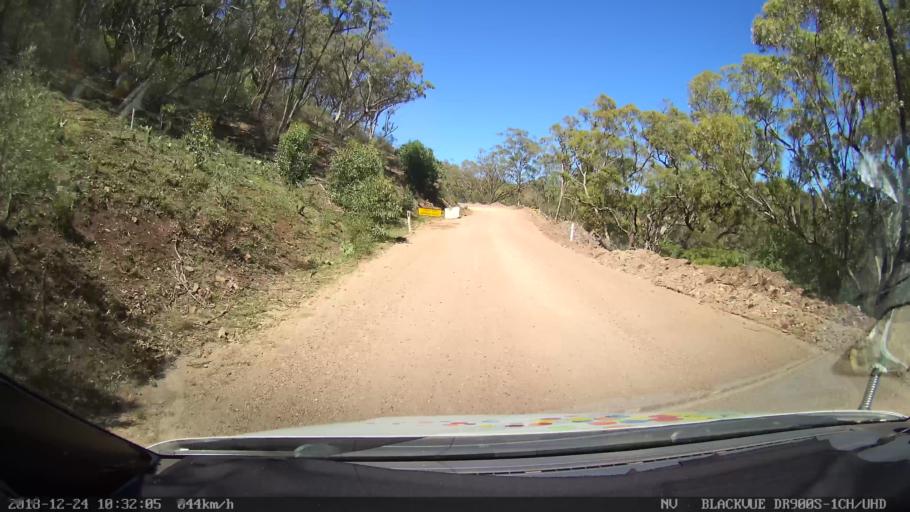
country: AU
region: New South Wales
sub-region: Upper Hunter Shire
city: Merriwa
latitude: -31.8402
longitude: 150.5179
